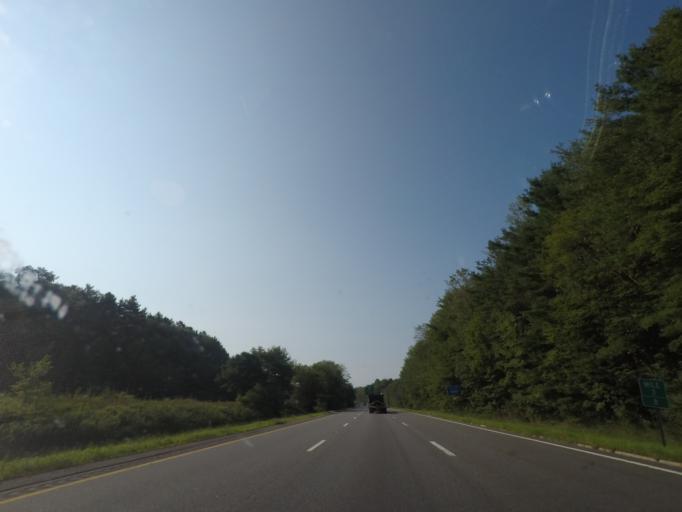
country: US
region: Massachusetts
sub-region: Worcester County
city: Webster
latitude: 42.0776
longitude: -71.8661
